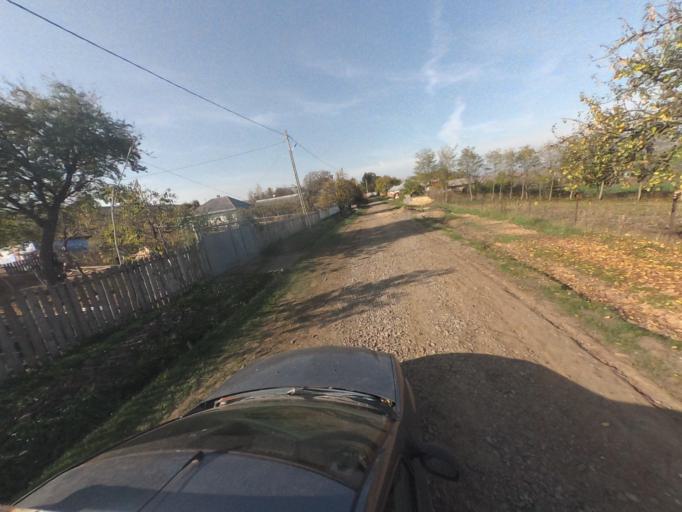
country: RO
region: Vaslui
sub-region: Comuna Bacesti
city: Bacesti
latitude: 46.8745
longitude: 27.1961
